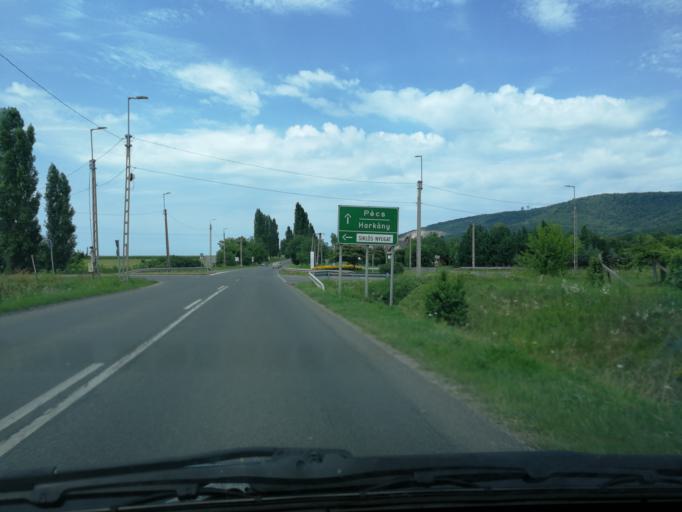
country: HU
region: Baranya
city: Siklos
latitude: 45.8682
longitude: 18.2831
